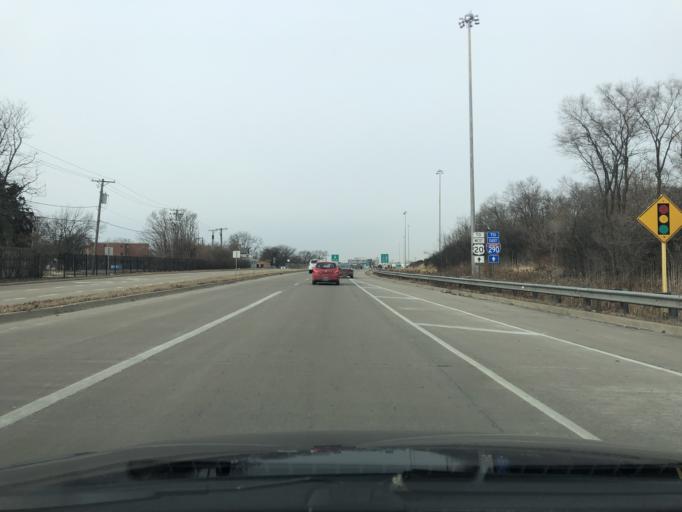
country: US
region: Illinois
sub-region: DuPage County
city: Elmhurst
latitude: 41.9129
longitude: -87.9409
